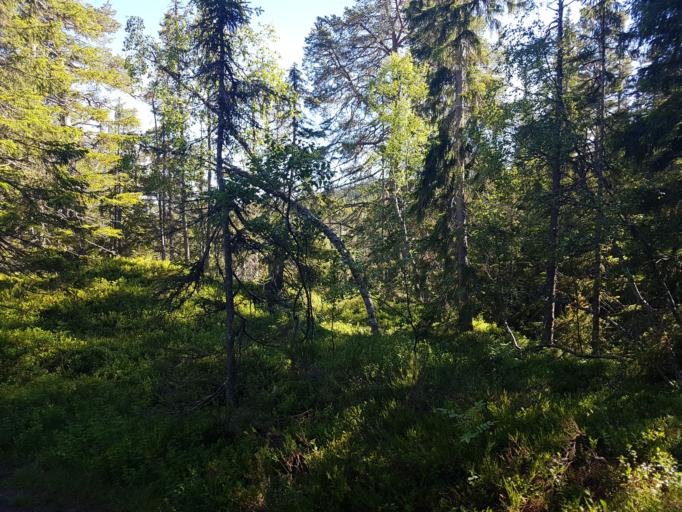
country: NO
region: Sor-Trondelag
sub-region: Trondheim
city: Trondheim
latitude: 63.4382
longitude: 10.2692
